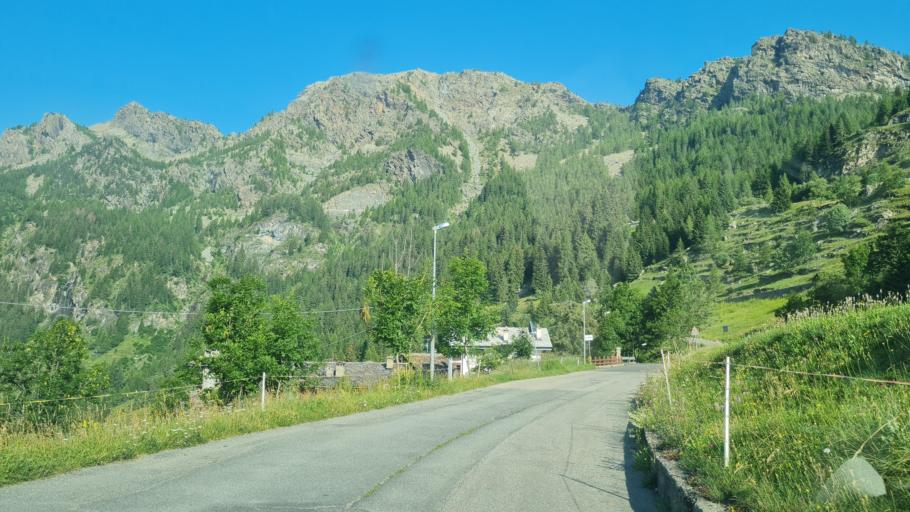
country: IT
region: Aosta Valley
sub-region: Valle d'Aosta
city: Champorcher
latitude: 45.6253
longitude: 7.6093
